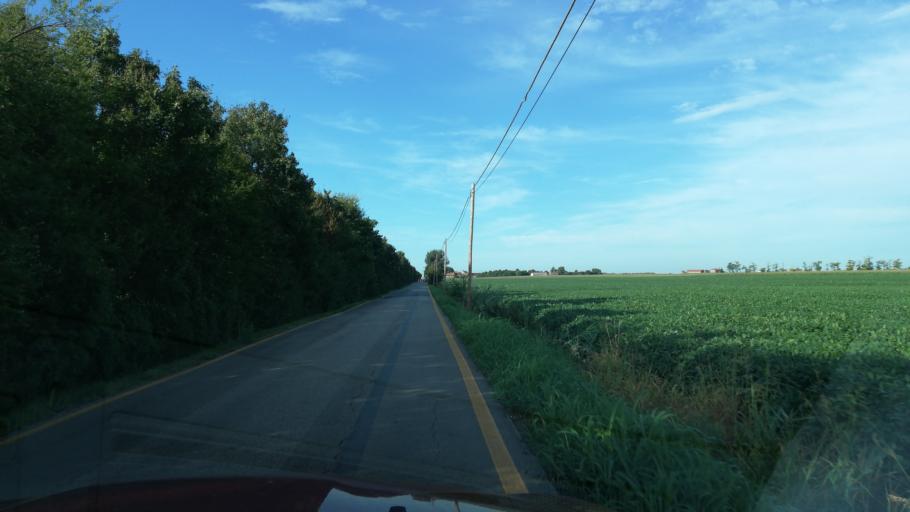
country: IT
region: Veneto
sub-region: Provincia di Venezia
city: San Giorgio di Livenza
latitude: 45.6373
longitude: 12.7877
